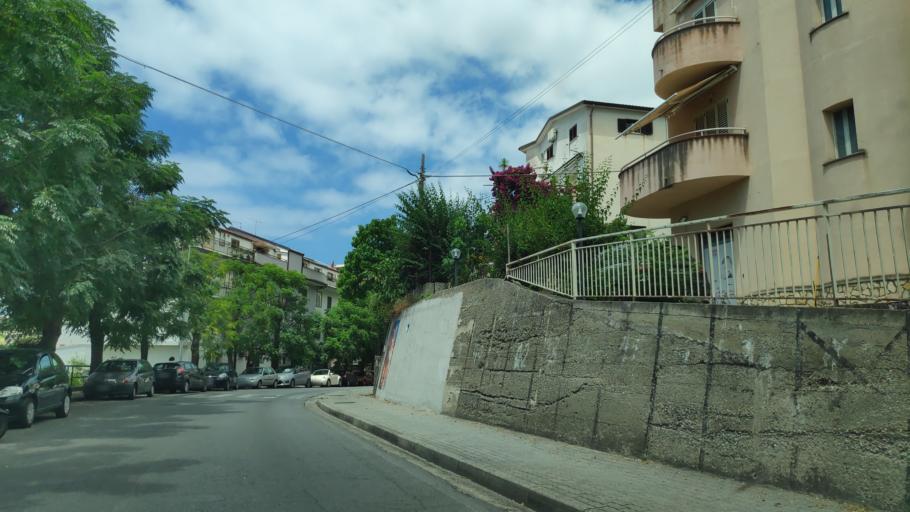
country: IT
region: Calabria
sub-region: Provincia di Cosenza
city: Paola
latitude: 39.3600
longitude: 16.0364
